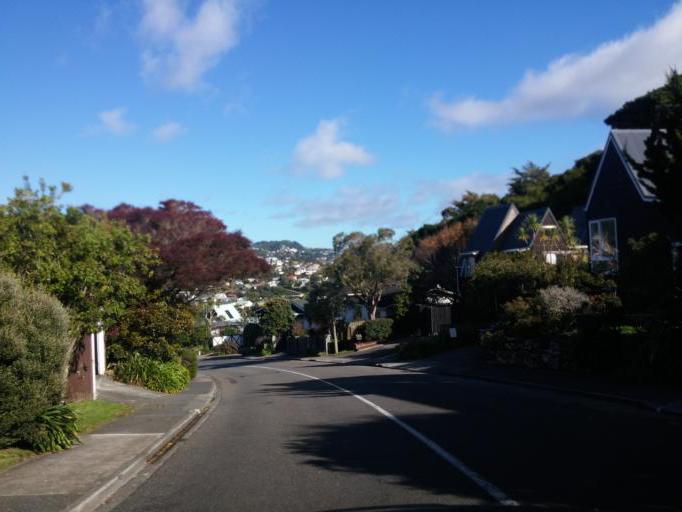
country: NZ
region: Wellington
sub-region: Wellington City
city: Kelburn
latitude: -41.2449
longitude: 174.7813
